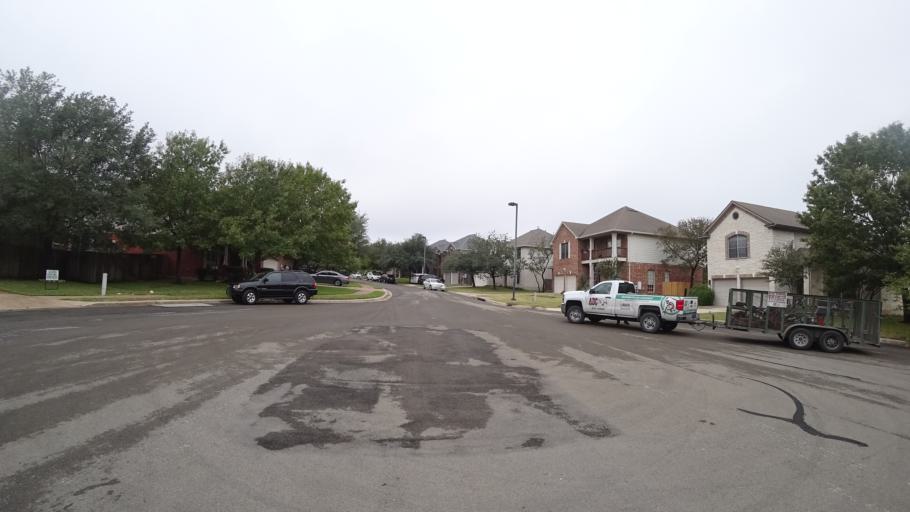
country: US
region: Texas
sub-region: Travis County
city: Shady Hollow
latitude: 30.1882
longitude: -97.8641
